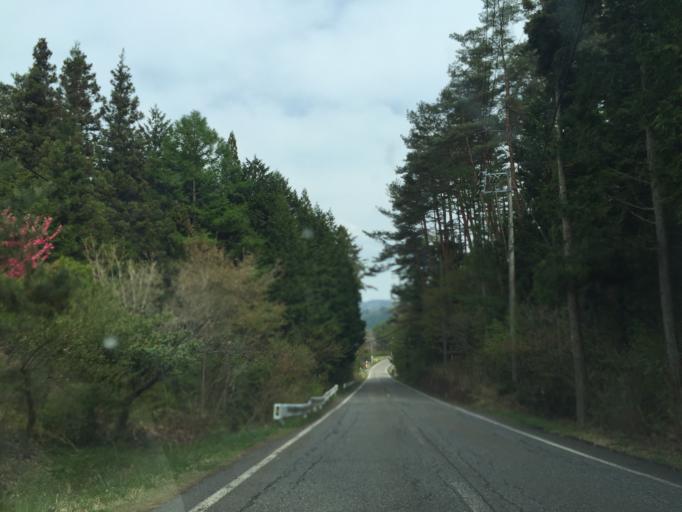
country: JP
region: Nagano
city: Iida
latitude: 35.2886
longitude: 137.6880
